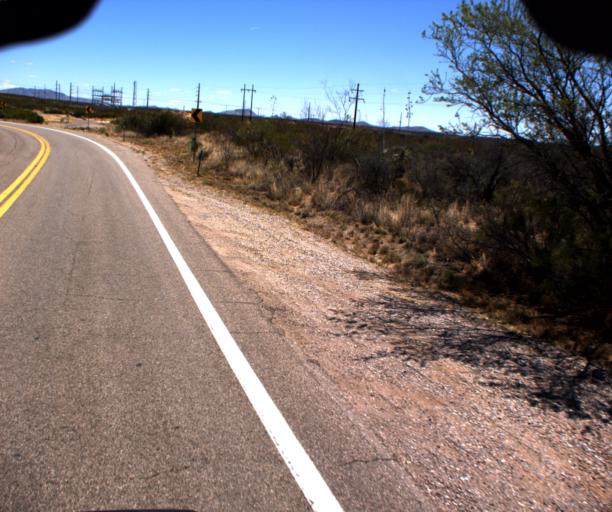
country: US
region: Arizona
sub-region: Cochise County
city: Tombstone
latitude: 31.7481
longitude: -110.0991
